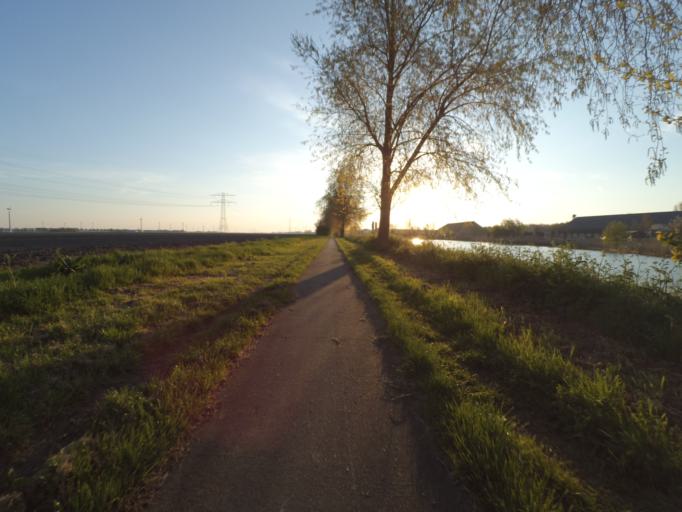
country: NL
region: Flevoland
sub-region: Gemeente Zeewolde
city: Zeewolde
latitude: 52.3575
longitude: 5.4917
